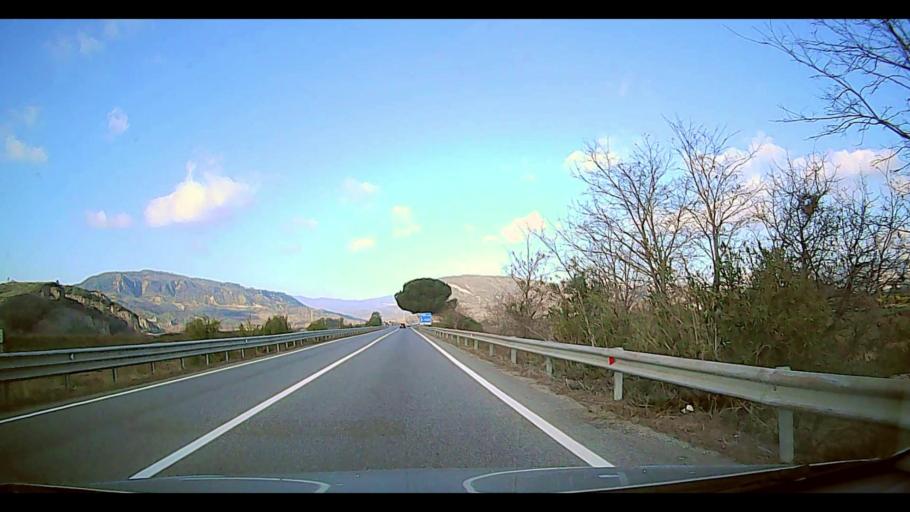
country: IT
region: Calabria
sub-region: Provincia di Crotone
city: Santa Severina
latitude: 39.1783
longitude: 16.9247
